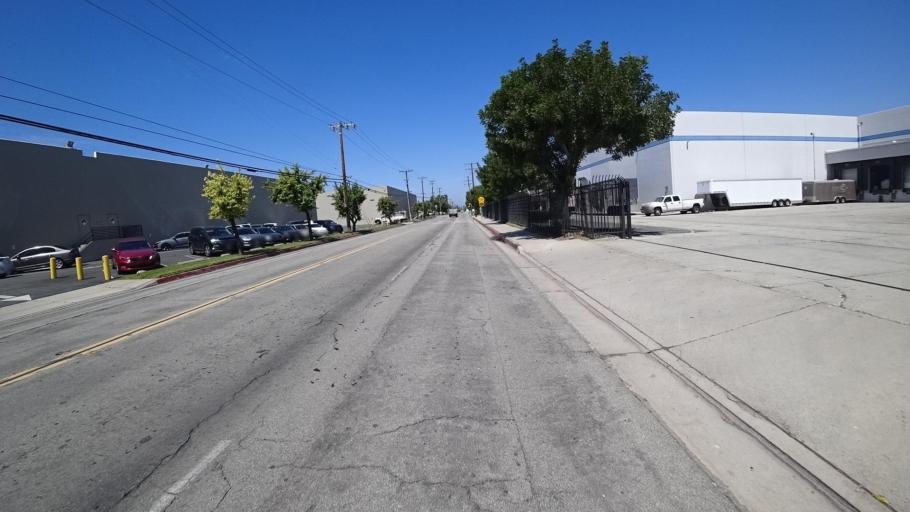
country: US
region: California
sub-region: Los Angeles County
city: Avocado Heights
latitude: 34.0246
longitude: -117.9738
